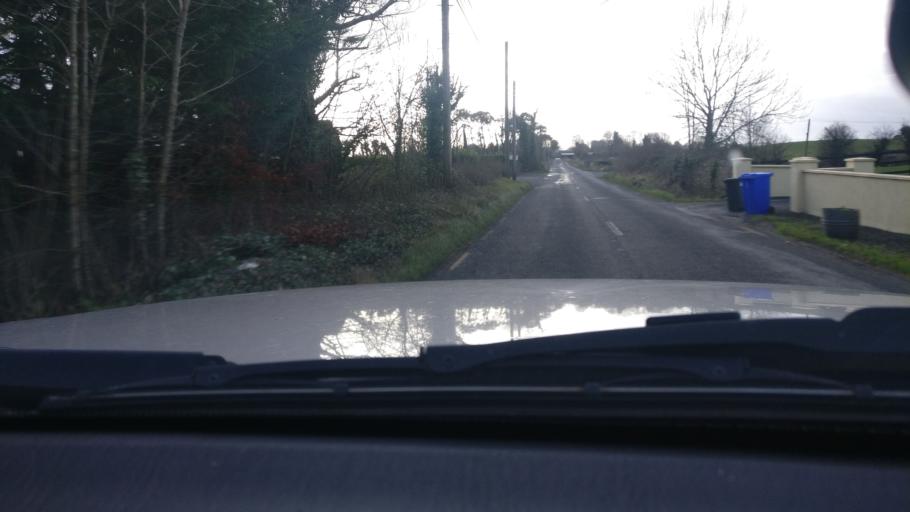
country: IE
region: Connaught
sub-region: County Galway
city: Ballinasloe
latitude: 53.2476
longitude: -8.2650
